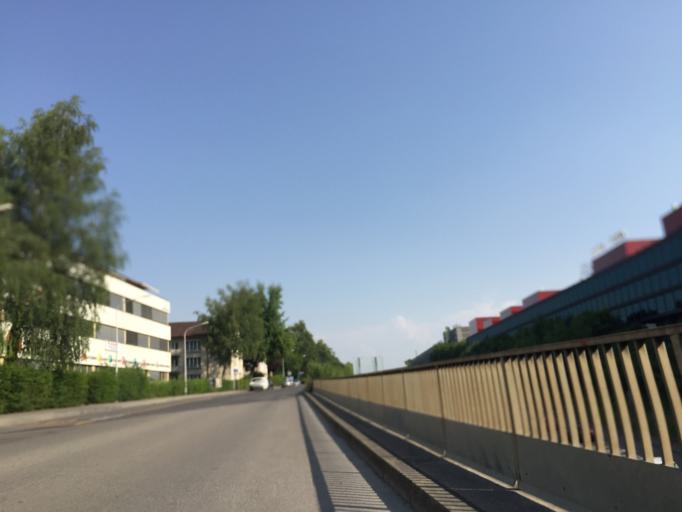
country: CH
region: Bern
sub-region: Bern-Mittelland District
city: Bern
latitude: 46.9557
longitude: 7.4684
